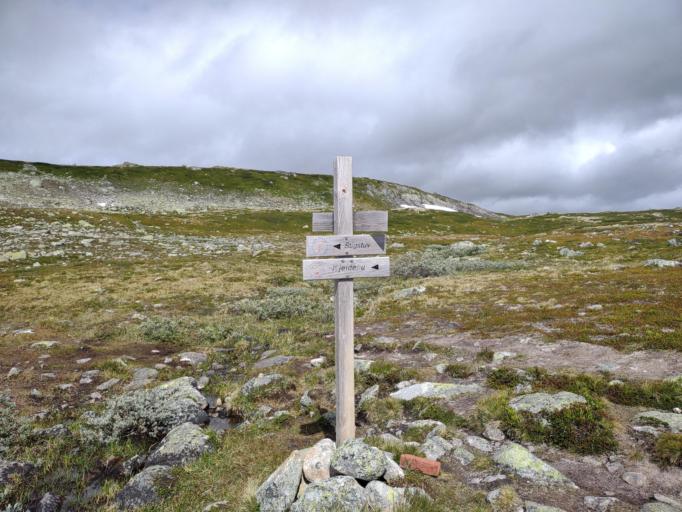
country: NO
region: Buskerud
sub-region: Hol
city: Geilo
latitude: 60.4529
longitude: 7.7102
